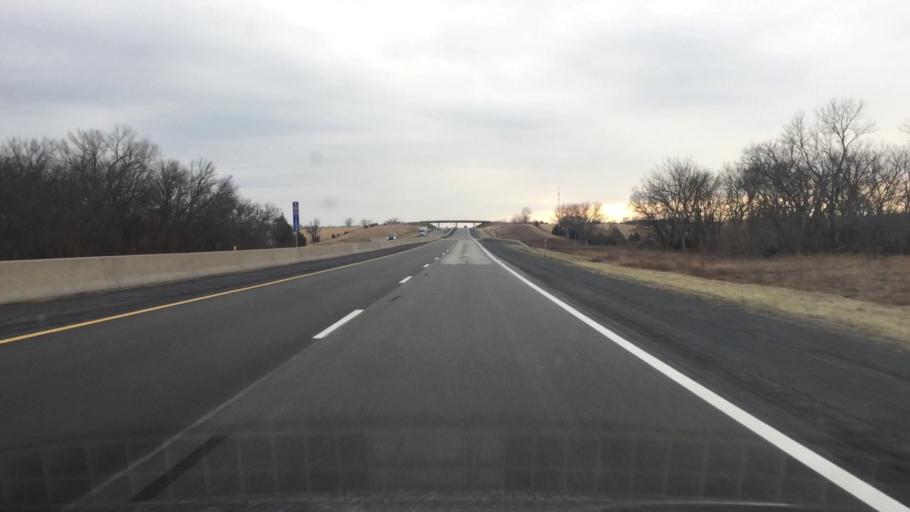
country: US
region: Kansas
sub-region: Osage County
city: Osage City
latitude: 38.7525
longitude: -95.9403
